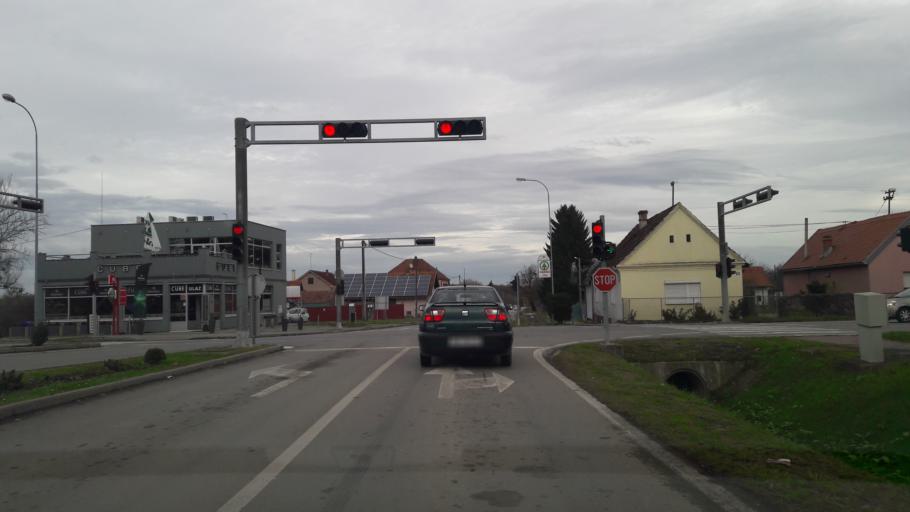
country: HR
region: Virovitick-Podravska
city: Orahovica
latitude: 45.5483
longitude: 17.9022
